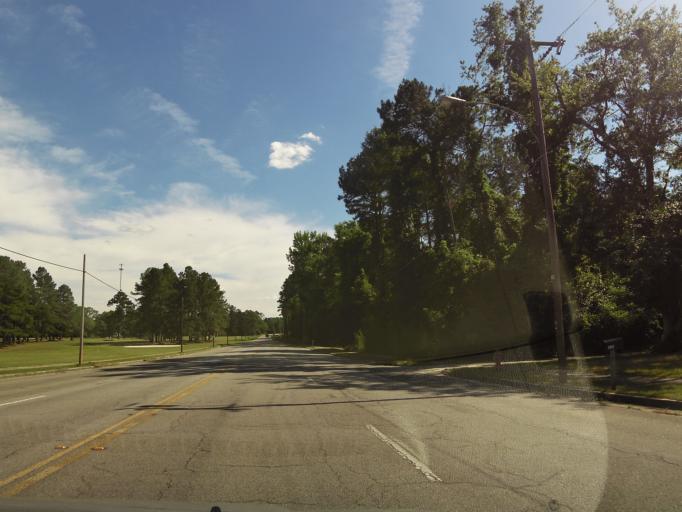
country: US
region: South Carolina
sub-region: Bamberg County
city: Denmark
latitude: 33.2998
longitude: -81.1457
